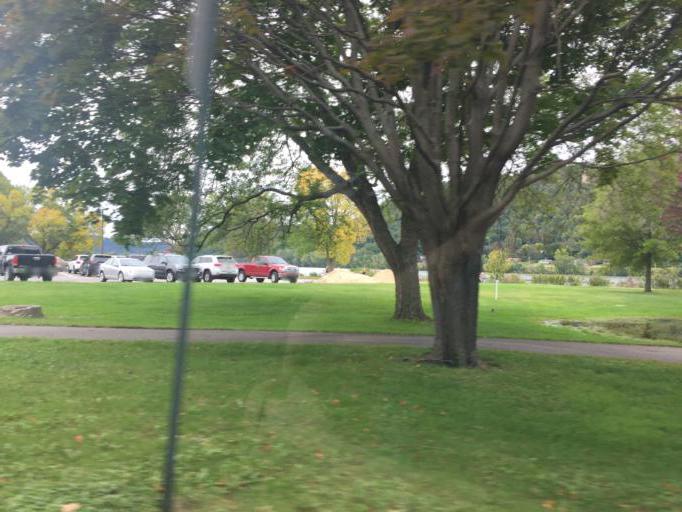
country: US
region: Minnesota
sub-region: Winona County
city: Winona
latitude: 44.0403
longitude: -91.6372
